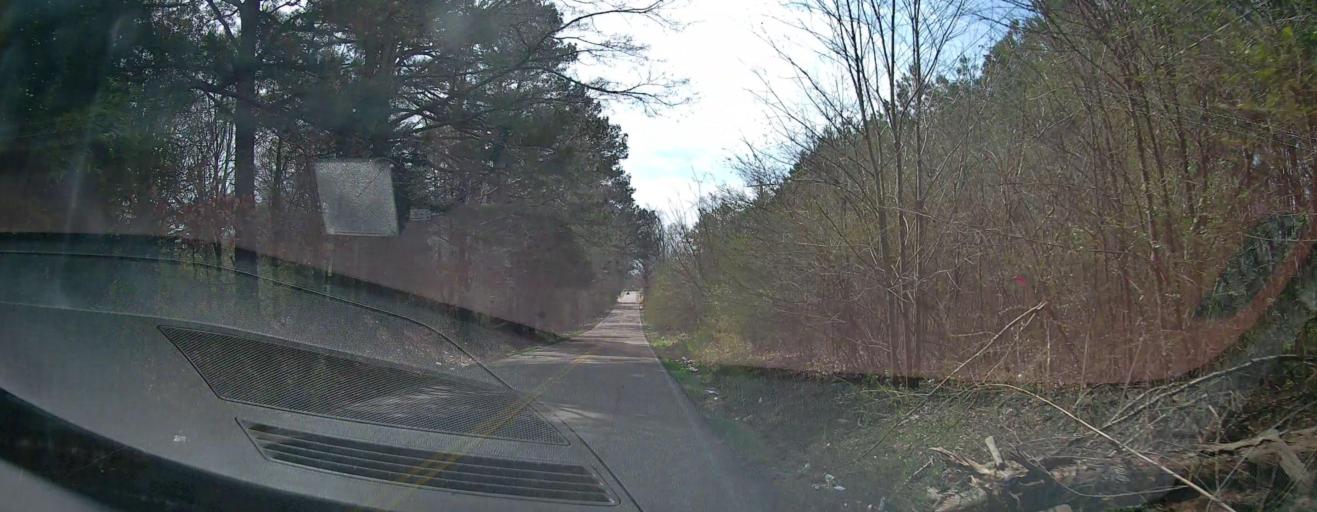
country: US
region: Mississippi
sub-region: De Soto County
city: Olive Branch
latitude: 34.9974
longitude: -89.8484
